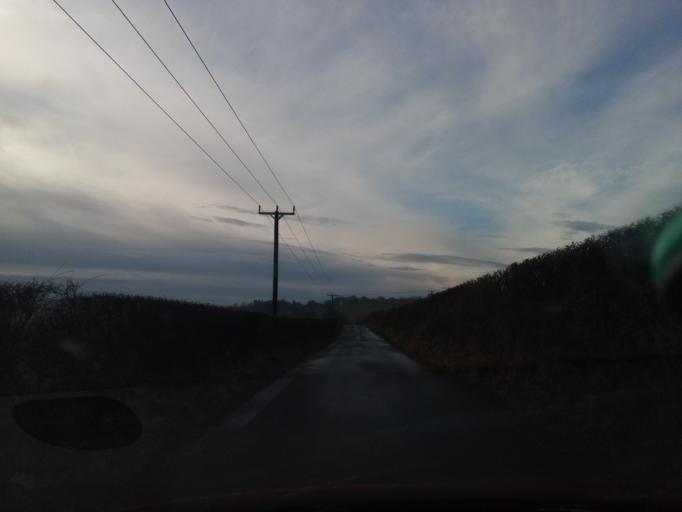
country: GB
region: Scotland
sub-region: The Scottish Borders
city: Hawick
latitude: 55.4486
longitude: -2.7408
